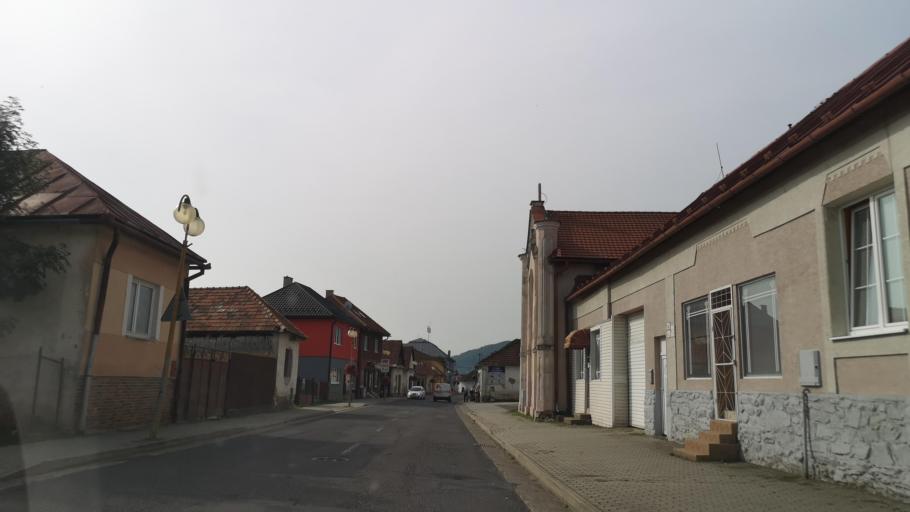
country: SK
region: Banskobystricky
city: Tisovec
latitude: 48.5730
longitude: 19.8404
